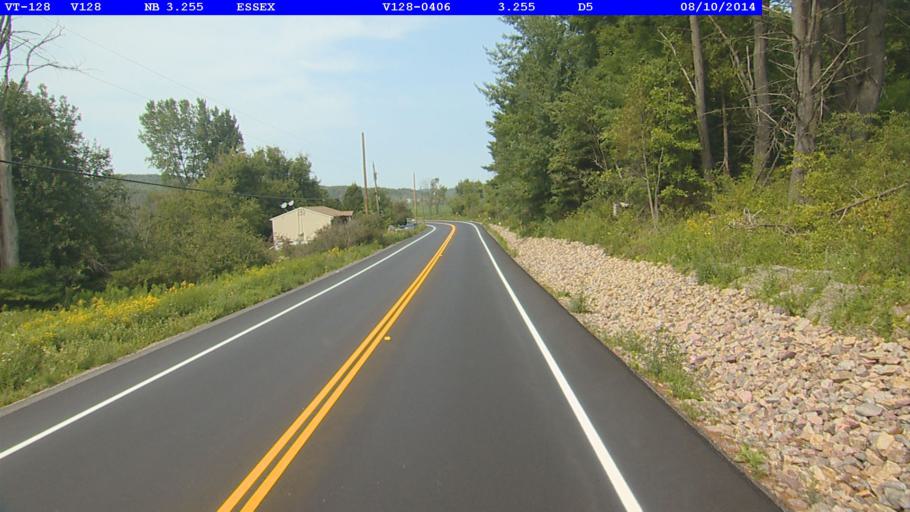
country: US
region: Vermont
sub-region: Chittenden County
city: Jericho
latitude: 44.5445
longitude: -73.0330
